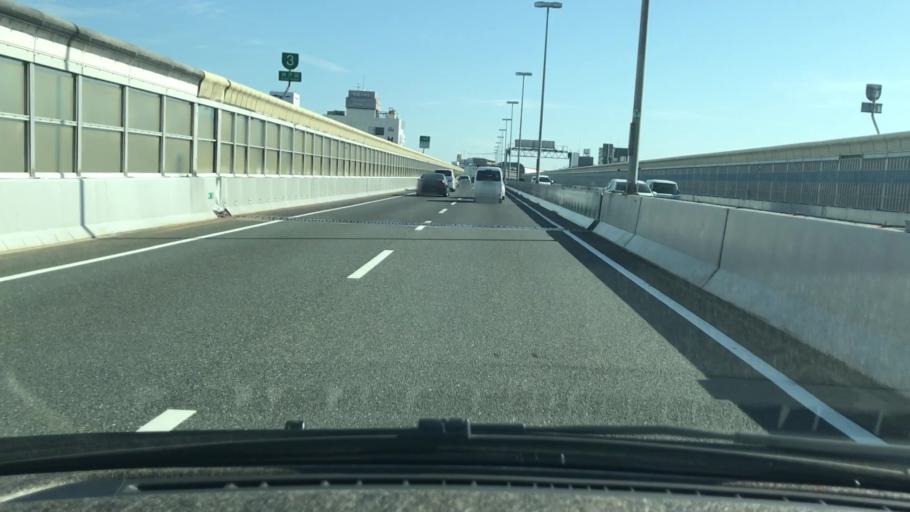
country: JP
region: Hyogo
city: Nishinomiya-hama
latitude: 34.7337
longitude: 135.3389
